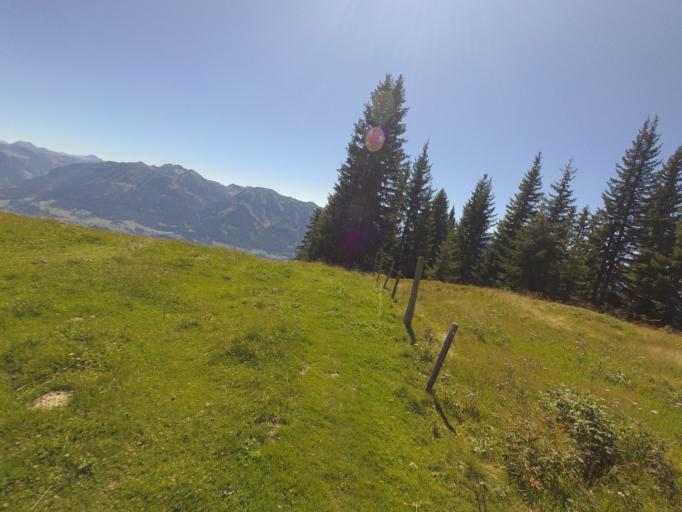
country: AT
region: Salzburg
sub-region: Politischer Bezirk Sankt Johann im Pongau
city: Goldegg
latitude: 47.3451
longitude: 13.0655
